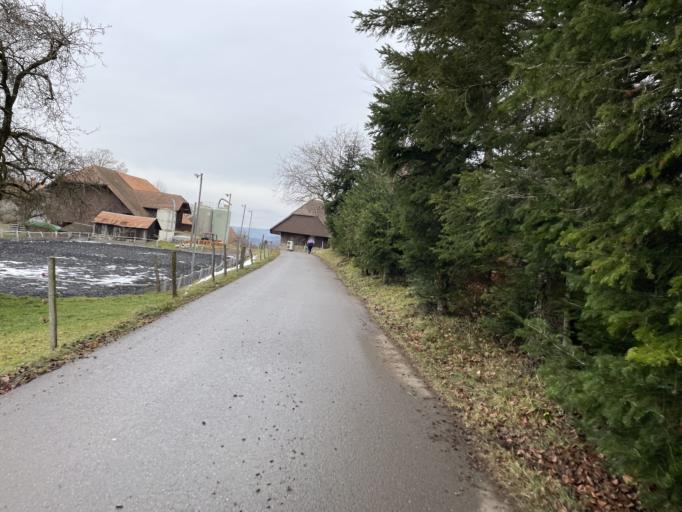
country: CH
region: Bern
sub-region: Bern-Mittelland District
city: Munsingen
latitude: 46.8593
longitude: 7.5359
